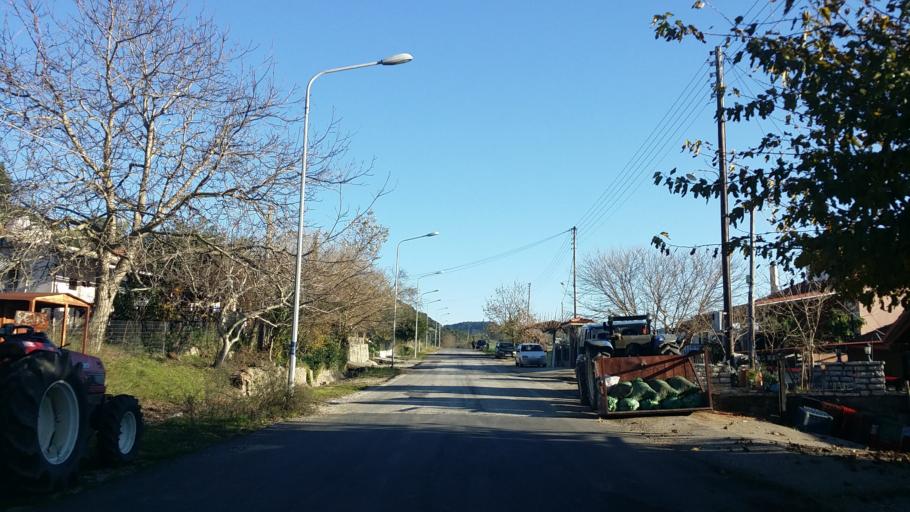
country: GR
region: West Greece
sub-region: Nomos Aitolias kai Akarnanias
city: Sardinia
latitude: 38.8749
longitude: 21.2525
